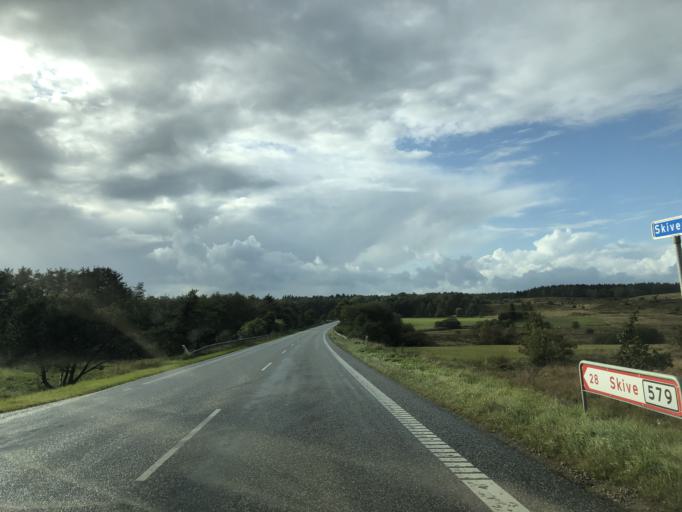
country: DK
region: North Denmark
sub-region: Vesthimmerland Kommune
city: Alestrup
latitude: 56.6115
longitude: 9.4352
